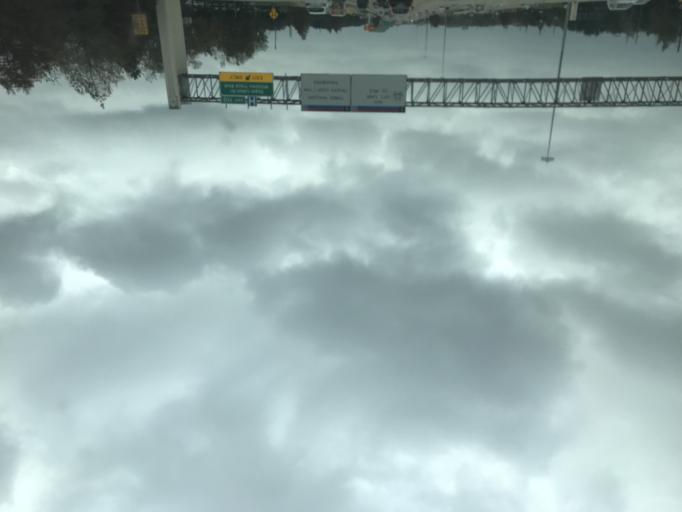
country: US
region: Texas
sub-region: Fort Bend County
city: Sugar Land
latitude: 29.5990
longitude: -95.6217
